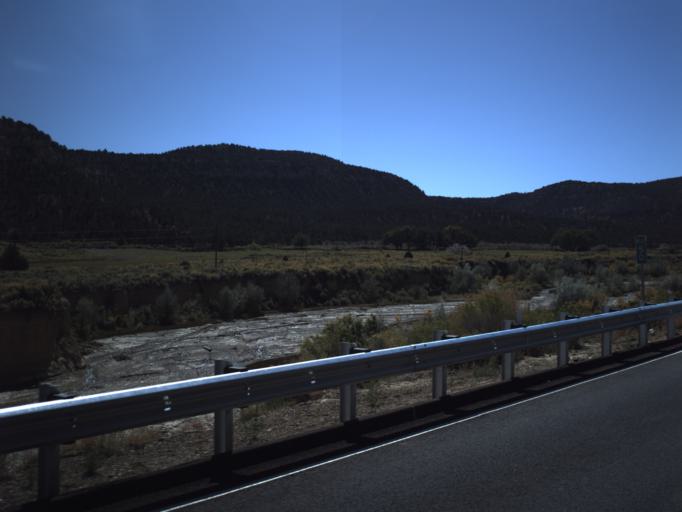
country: US
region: Utah
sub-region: Wayne County
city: Loa
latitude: 37.7357
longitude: -111.7491
